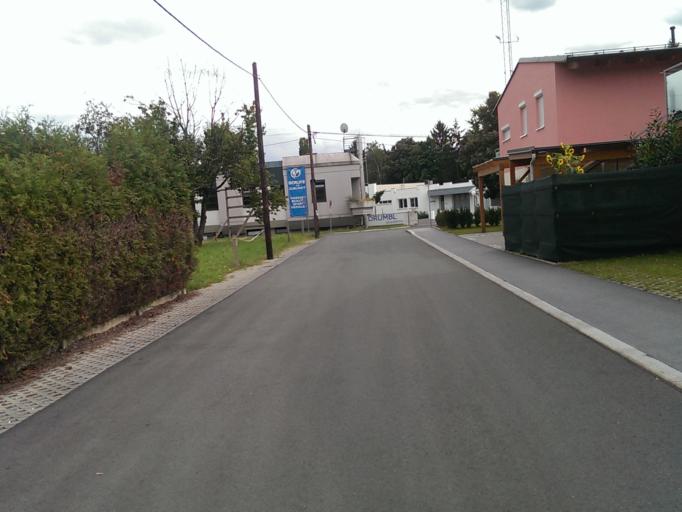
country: AT
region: Styria
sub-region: Graz Stadt
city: Graz
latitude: 47.0479
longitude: 15.4601
